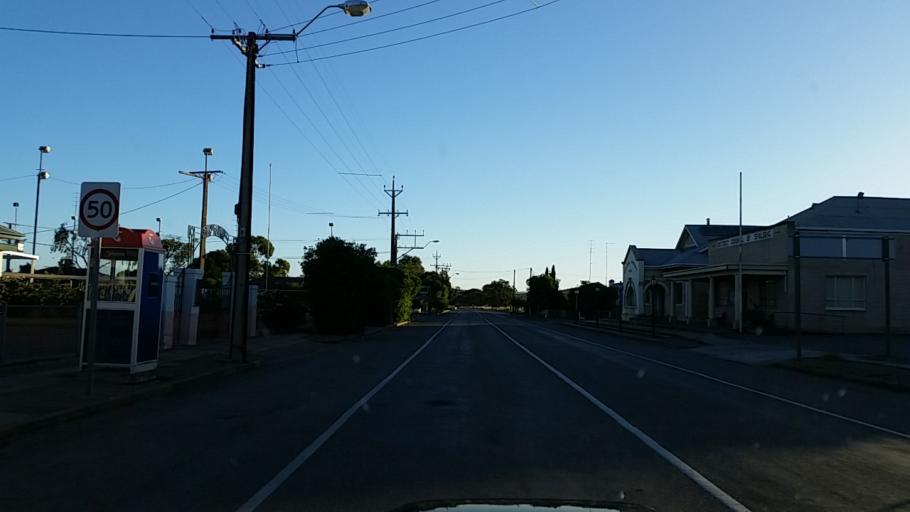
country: AU
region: South Australia
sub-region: Northern Areas
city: Jamestown
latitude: -33.4994
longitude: 138.6074
